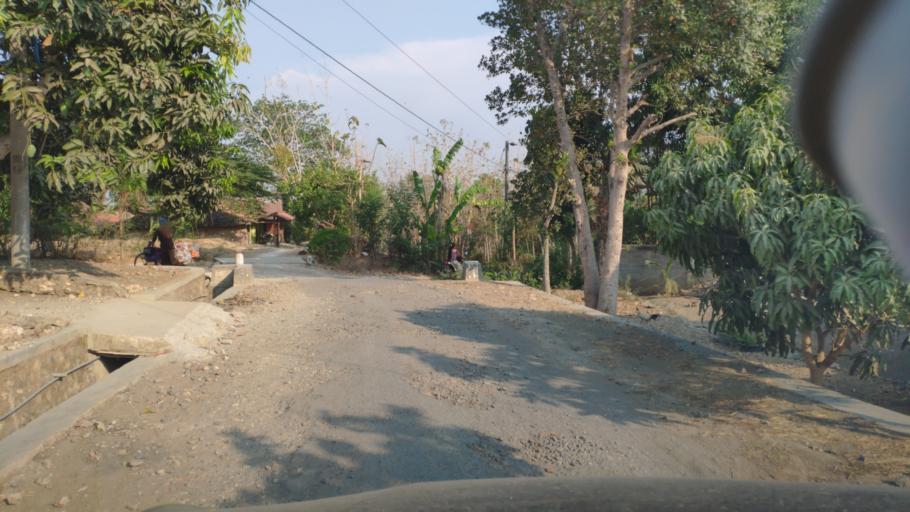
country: ID
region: Central Java
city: Wanutengah
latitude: -6.9288
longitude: 111.5298
